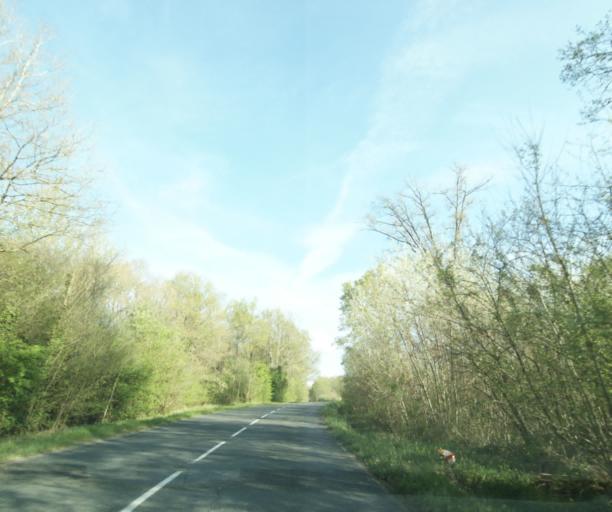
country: FR
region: Ile-de-France
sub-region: Departement de Seine-et-Marne
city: Vernou-la-Celle-sur-Seine
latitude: 48.4664
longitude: 2.8680
